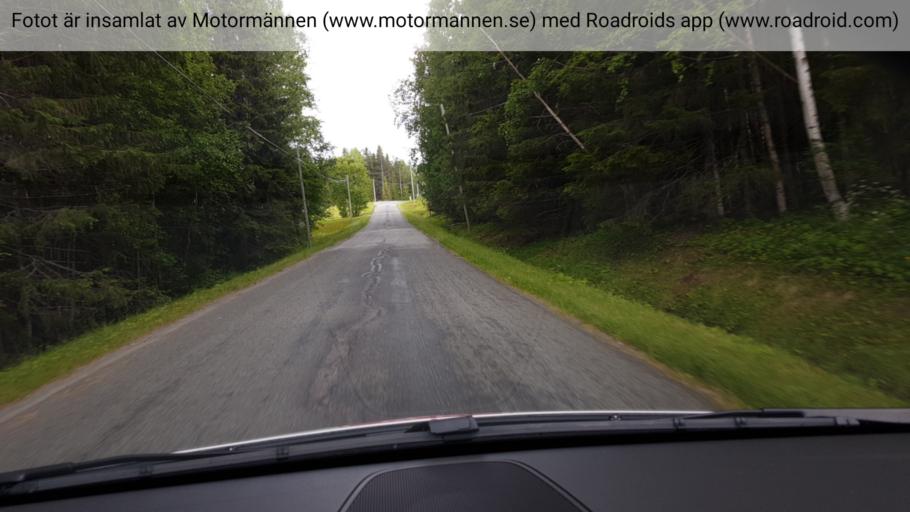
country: SE
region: Vaesterbotten
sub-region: Dorotea Kommun
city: Dorotea
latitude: 64.1231
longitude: 16.3104
